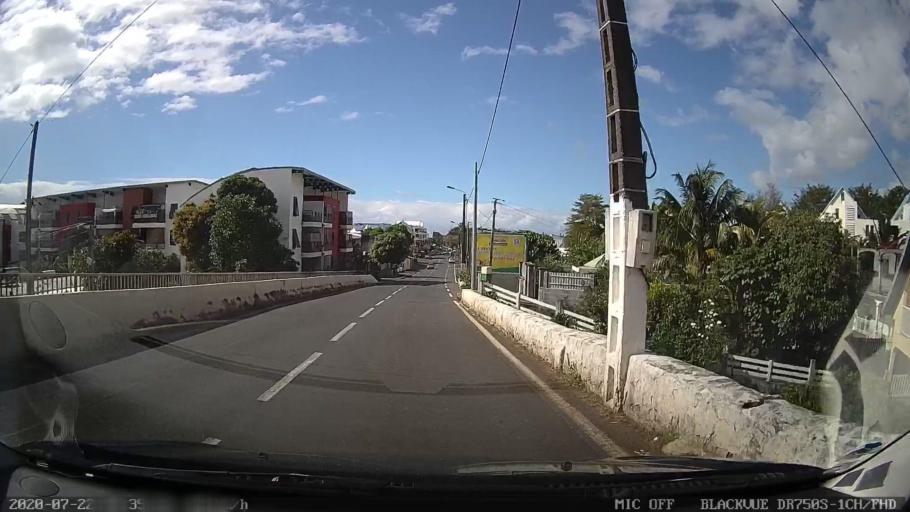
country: RE
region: Reunion
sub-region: Reunion
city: Sainte-Suzanne
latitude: -20.9046
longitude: 55.6046
